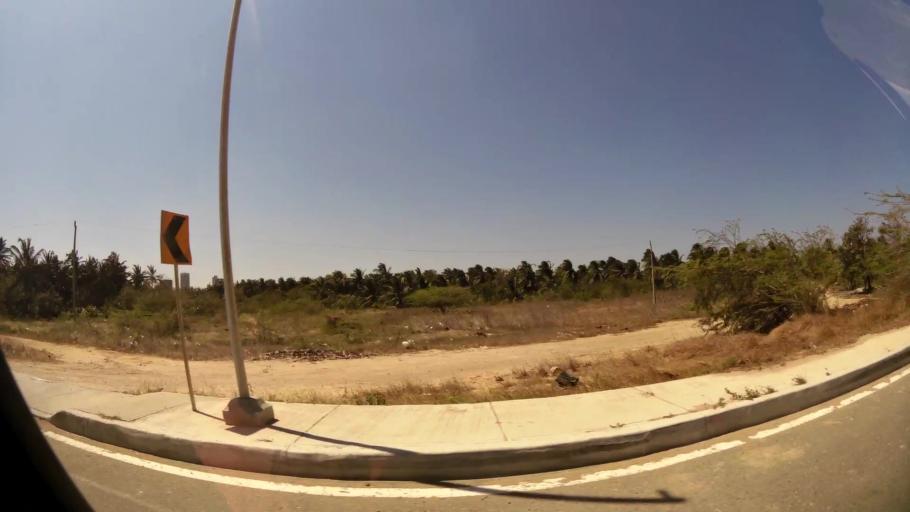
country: CO
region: Atlantico
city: Barranquilla
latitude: 10.9898
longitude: -74.7719
